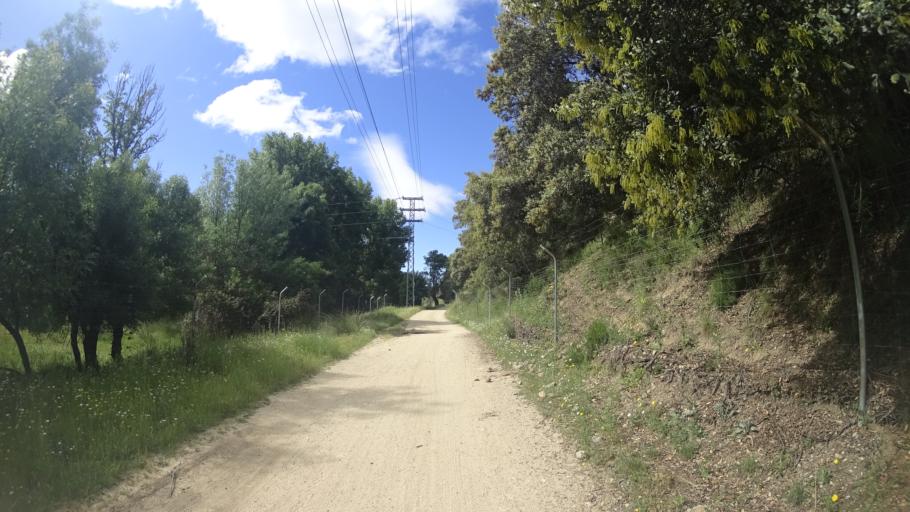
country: ES
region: Madrid
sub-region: Provincia de Madrid
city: Villanueva del Pardillo
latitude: 40.4340
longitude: -3.9527
